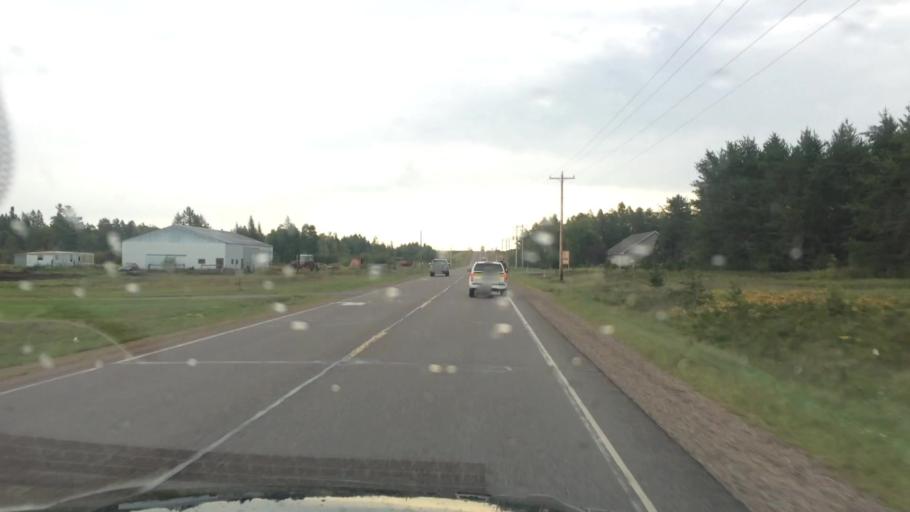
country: US
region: Wisconsin
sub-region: Lincoln County
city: Tomahawk
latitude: 45.4962
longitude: -89.7067
